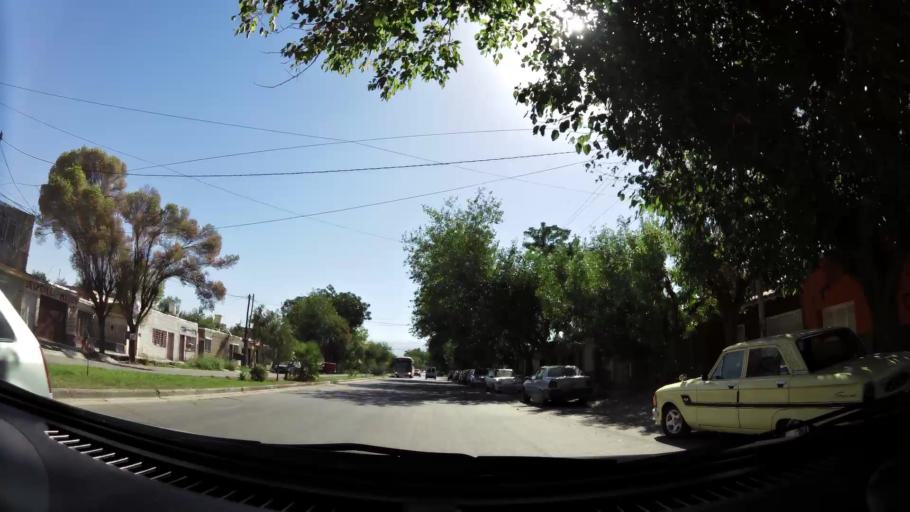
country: AR
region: Mendoza
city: Mendoza
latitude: -32.8810
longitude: -68.8033
